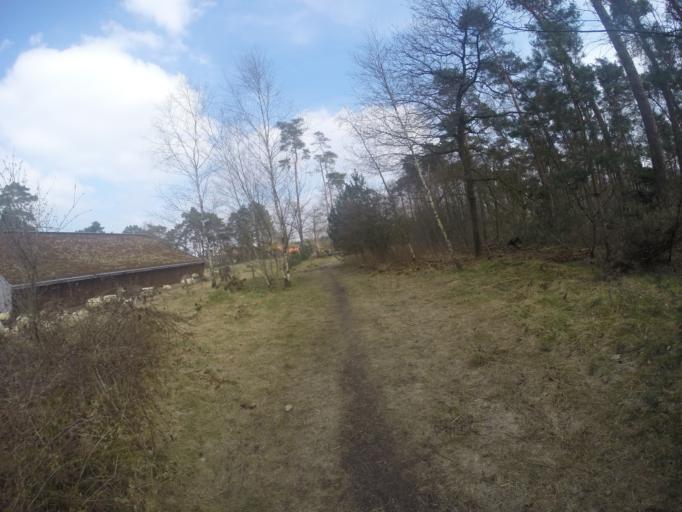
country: NL
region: Gelderland
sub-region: Gemeente Lochem
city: Almen
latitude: 52.1376
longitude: 6.3225
